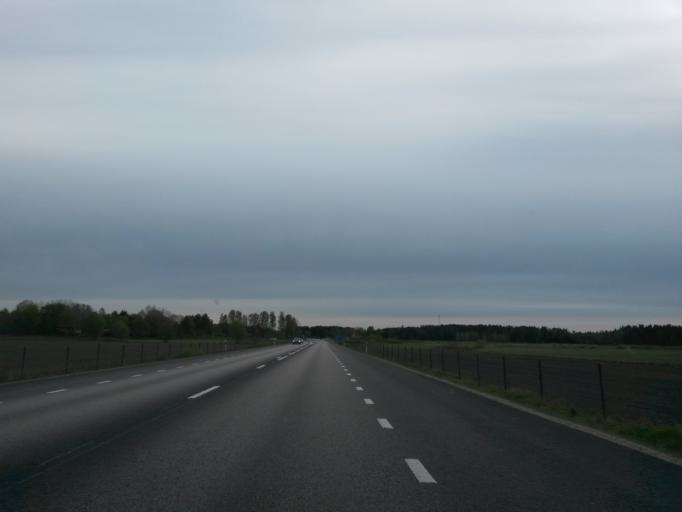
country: SE
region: Vaestra Goetaland
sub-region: Vara Kommun
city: Vara
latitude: 58.1738
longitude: 12.8905
